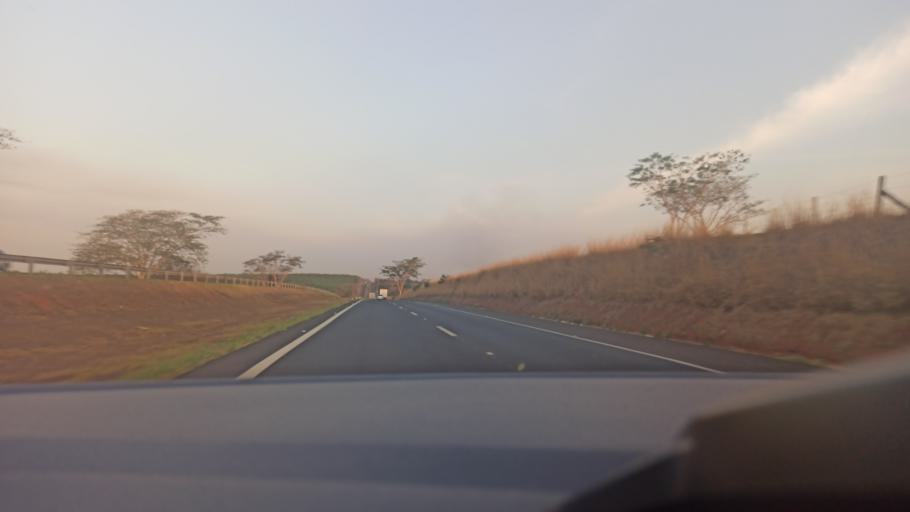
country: BR
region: Sao Paulo
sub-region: Taquaritinga
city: Taquaritinga
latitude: -21.4435
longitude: -48.6451
